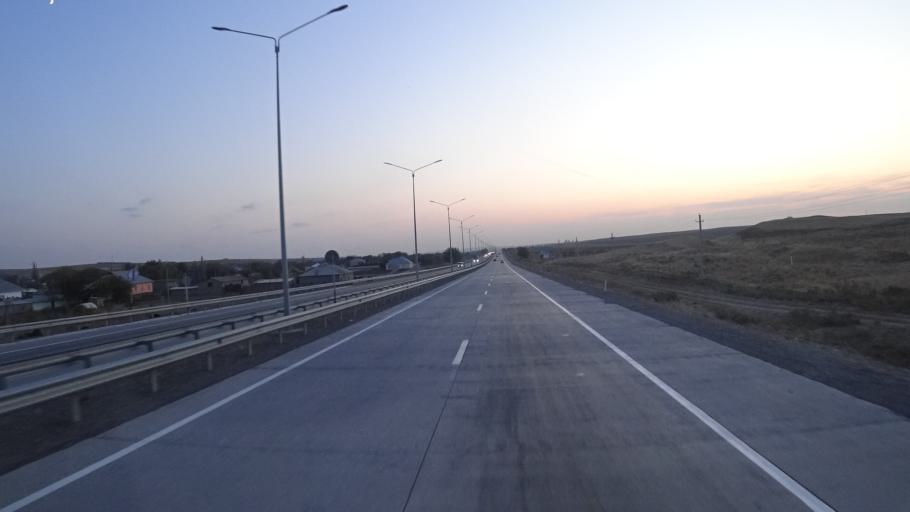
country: KZ
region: Ongtustik Qazaqstan
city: Qazyqurt
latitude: 41.8939
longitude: 69.4507
